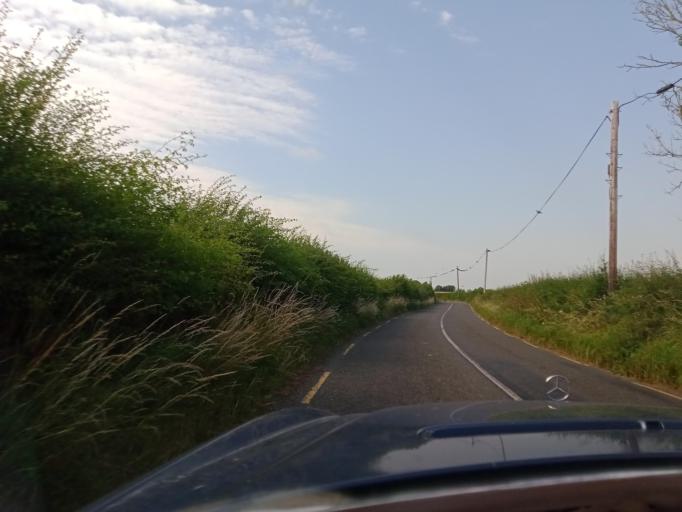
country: IE
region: Leinster
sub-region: Kilkenny
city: Callan
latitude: 52.5084
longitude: -7.3122
